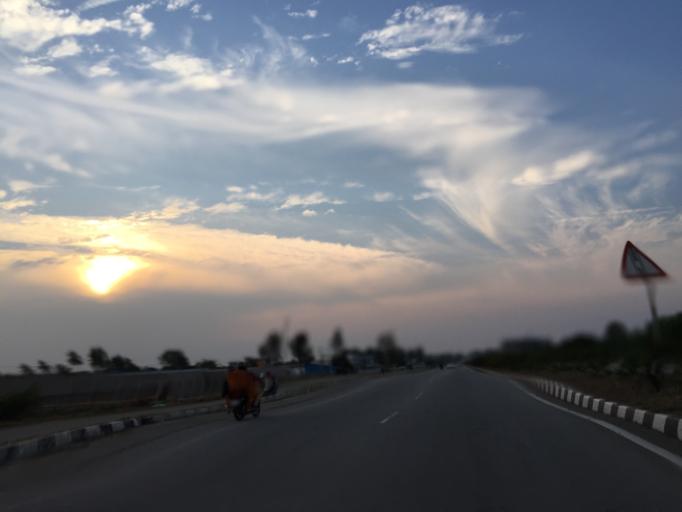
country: IN
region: Karnataka
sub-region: Kolar
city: Kolar
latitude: 13.1282
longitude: 77.9958
